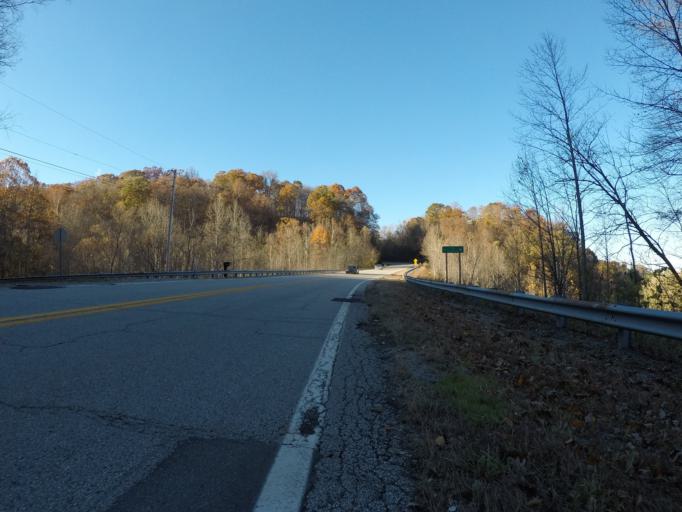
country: US
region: West Virginia
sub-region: Wayne County
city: Ceredo
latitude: 38.3796
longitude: -82.5631
